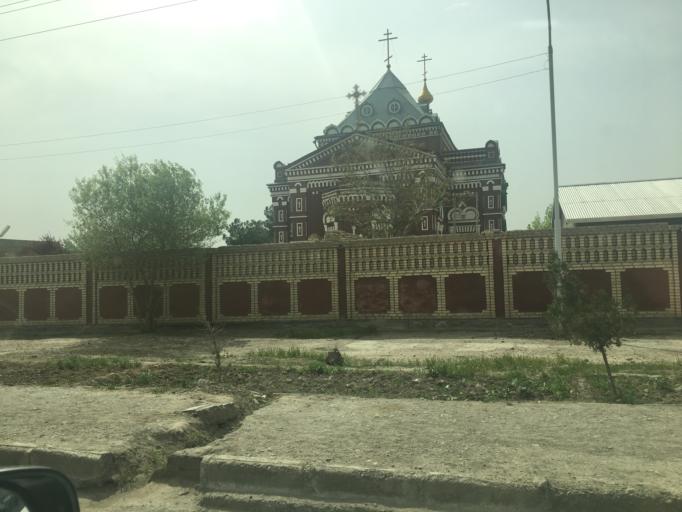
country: TM
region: Mary
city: Mary
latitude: 37.5979
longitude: 61.8550
